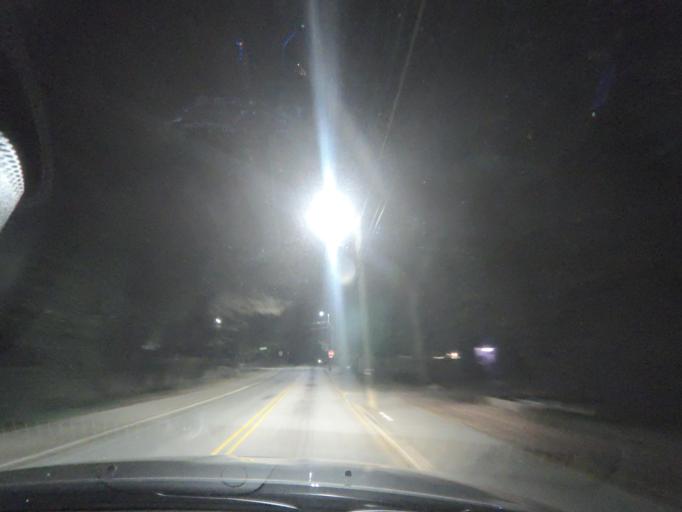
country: US
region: Georgia
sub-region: Fulton County
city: East Point
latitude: 33.6976
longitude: -84.4862
